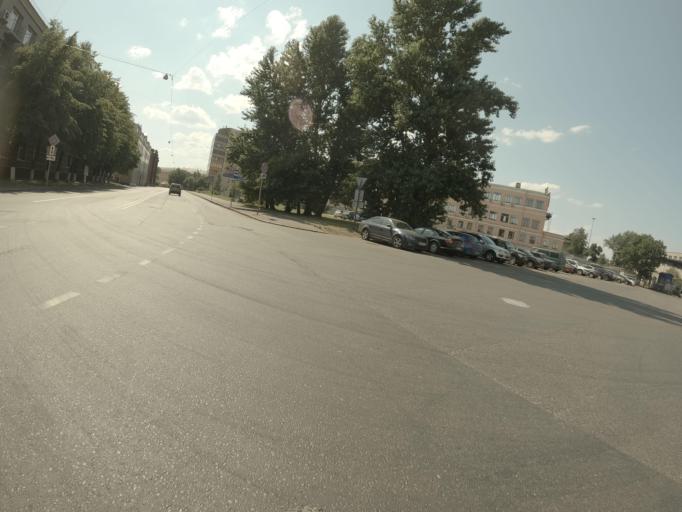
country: RU
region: St.-Petersburg
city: Admiralteisky
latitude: 59.9127
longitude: 30.2592
